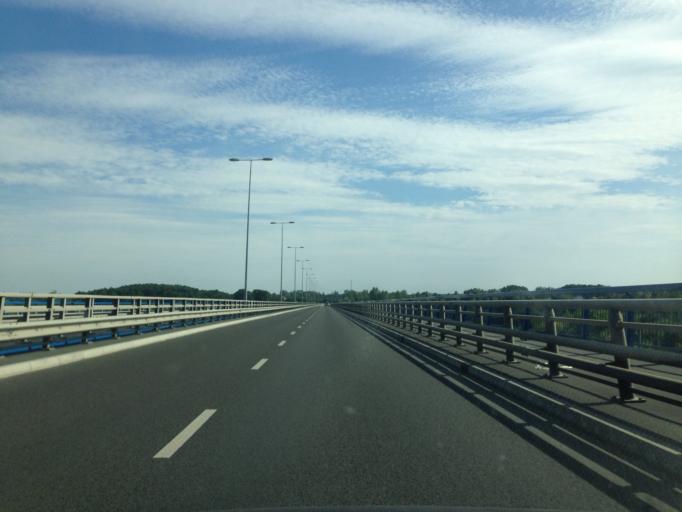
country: PL
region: Kujawsko-Pomorskie
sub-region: Torun
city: Torun
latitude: 53.0105
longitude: 18.6563
